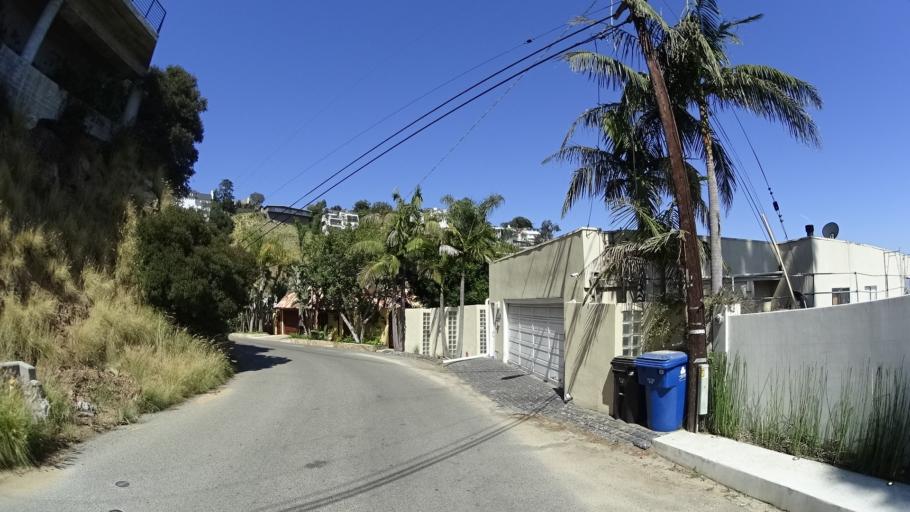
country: US
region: California
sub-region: Los Angeles County
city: West Hollywood
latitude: 34.1054
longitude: -118.3839
